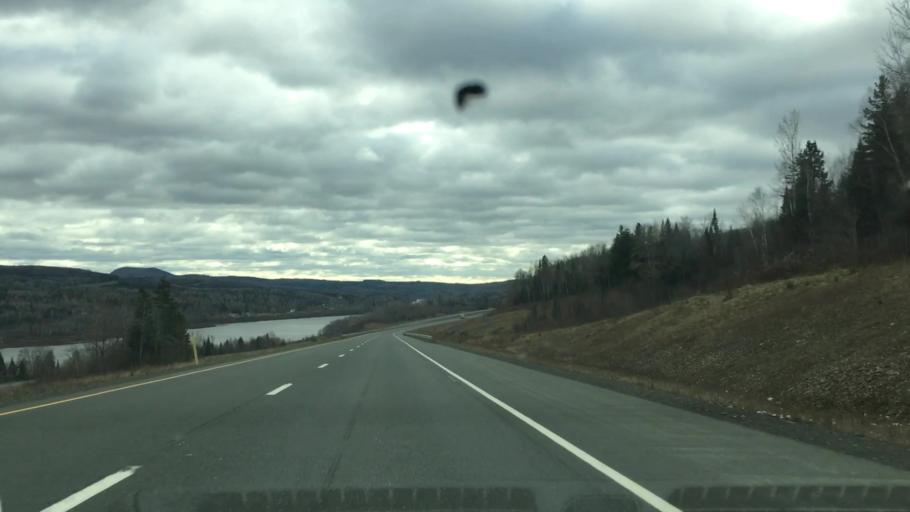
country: US
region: Maine
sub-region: Aroostook County
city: Fort Fairfield
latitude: 46.6839
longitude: -67.7336
